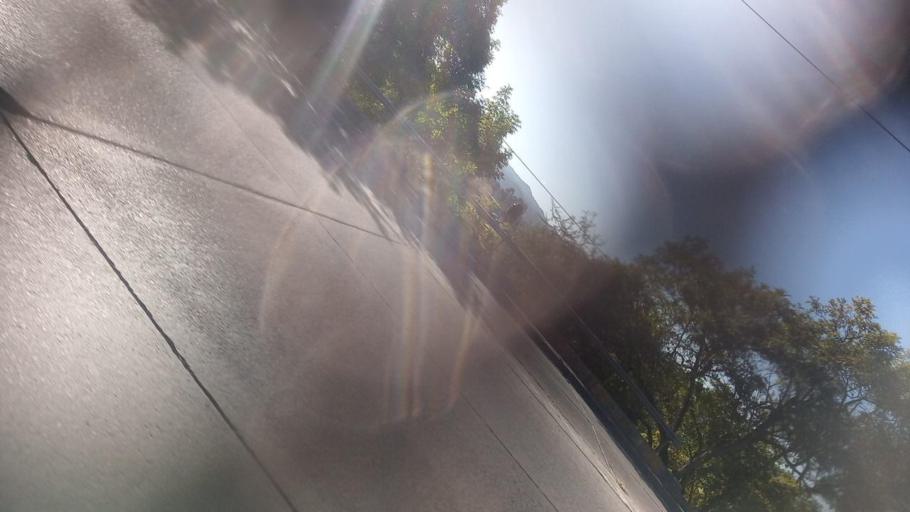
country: AR
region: Jujuy
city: San Salvador de Jujuy
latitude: -24.1775
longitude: -65.3091
